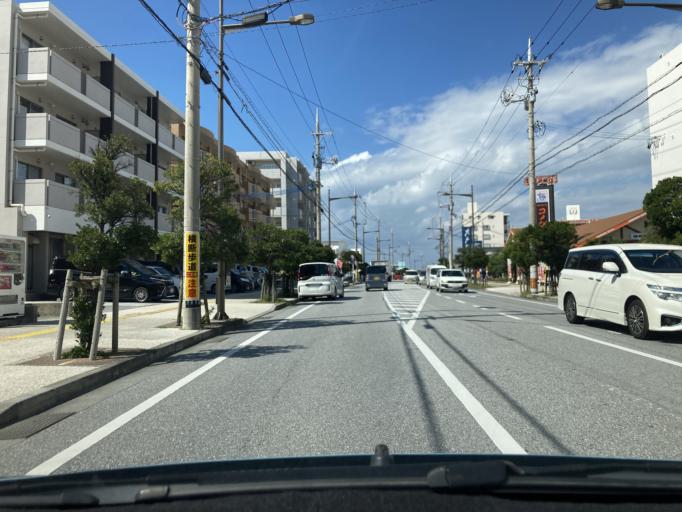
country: JP
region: Okinawa
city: Ginowan
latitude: 26.2701
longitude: 127.7319
